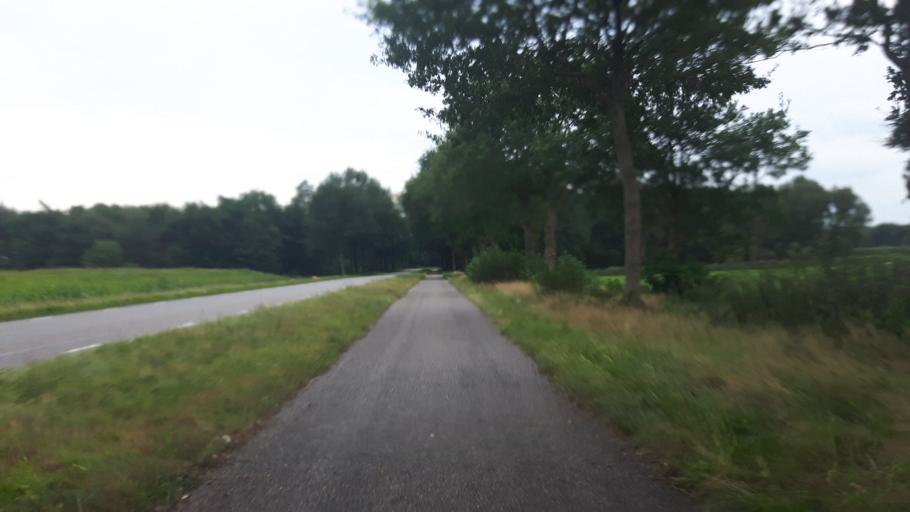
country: NL
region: Friesland
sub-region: Gemeente Heerenveen
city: Jubbega
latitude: 52.9662
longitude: 6.2207
